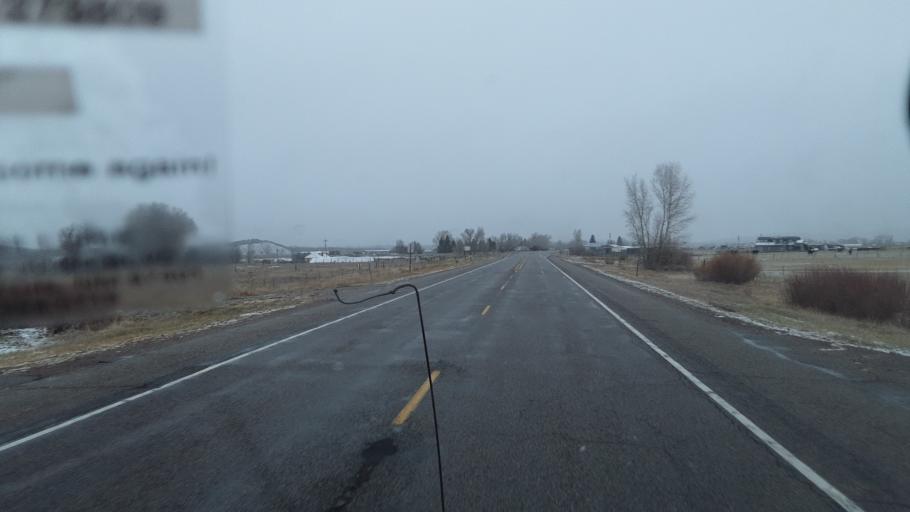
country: US
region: New Mexico
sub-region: Rio Arriba County
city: Tierra Amarilla
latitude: 36.7337
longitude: -106.5675
